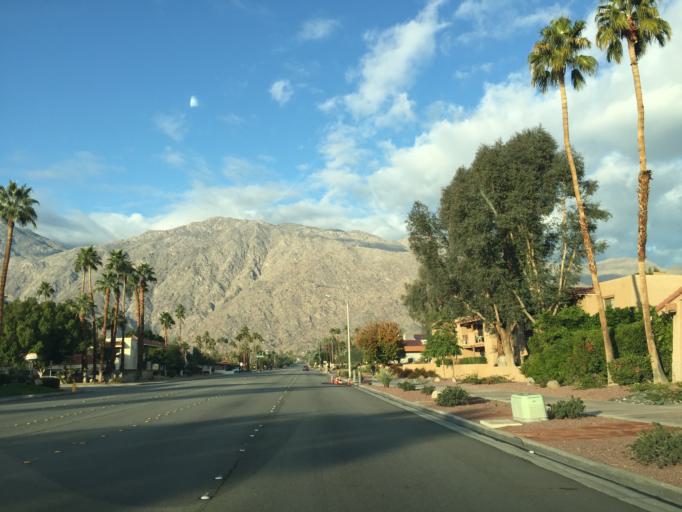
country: US
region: California
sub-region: Riverside County
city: Palm Springs
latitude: 33.8159
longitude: -116.5346
